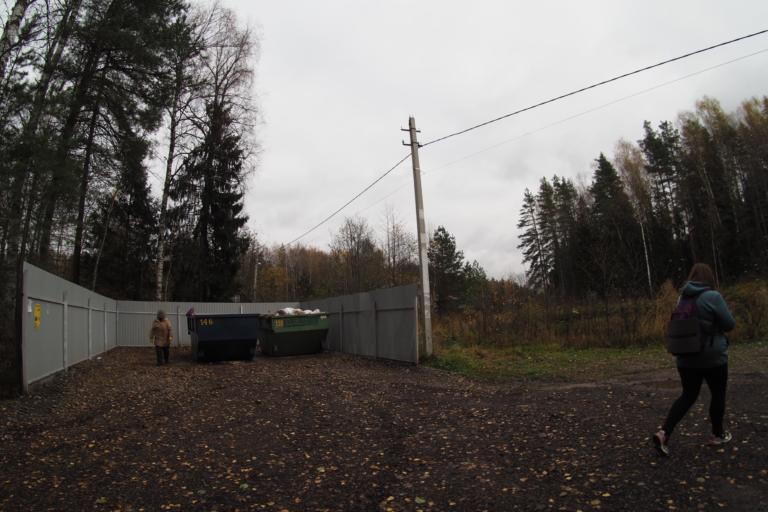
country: RU
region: Moskovskaya
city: Davydovo
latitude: 55.5686
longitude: 38.7567
